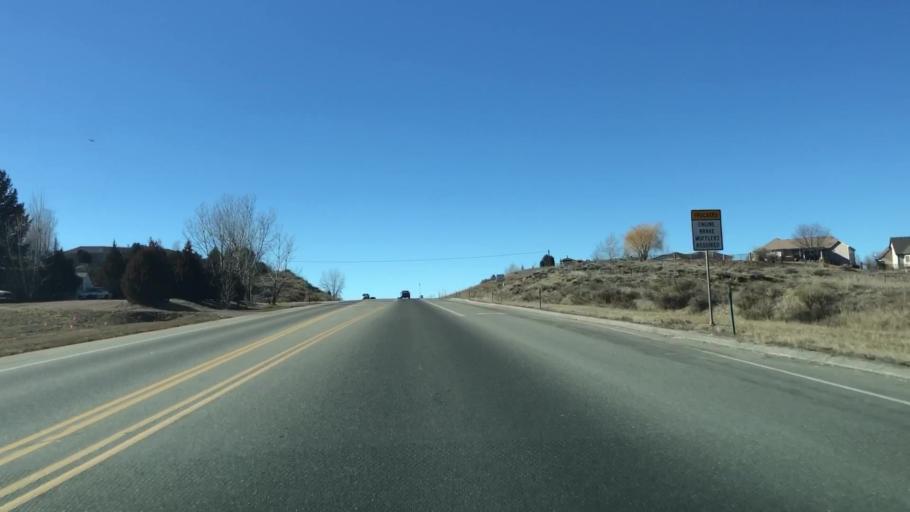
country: US
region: Colorado
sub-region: Weld County
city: Windsor
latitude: 40.4794
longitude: -104.9616
